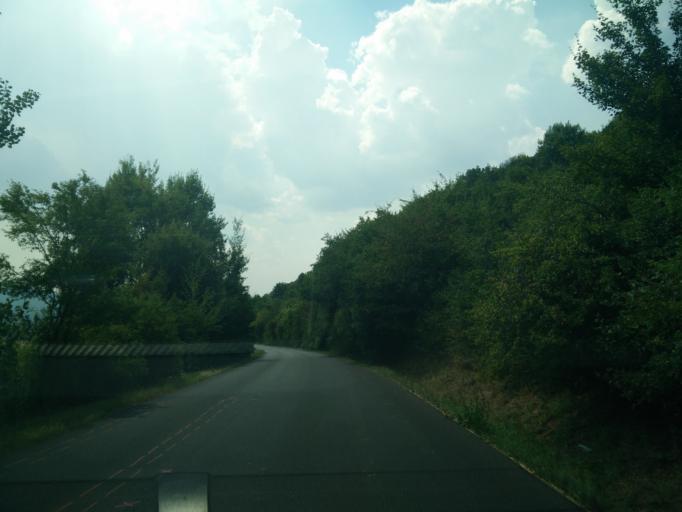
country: SK
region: Banskobystricky
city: Ziar nad Hronom
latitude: 48.5546
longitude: 18.7763
